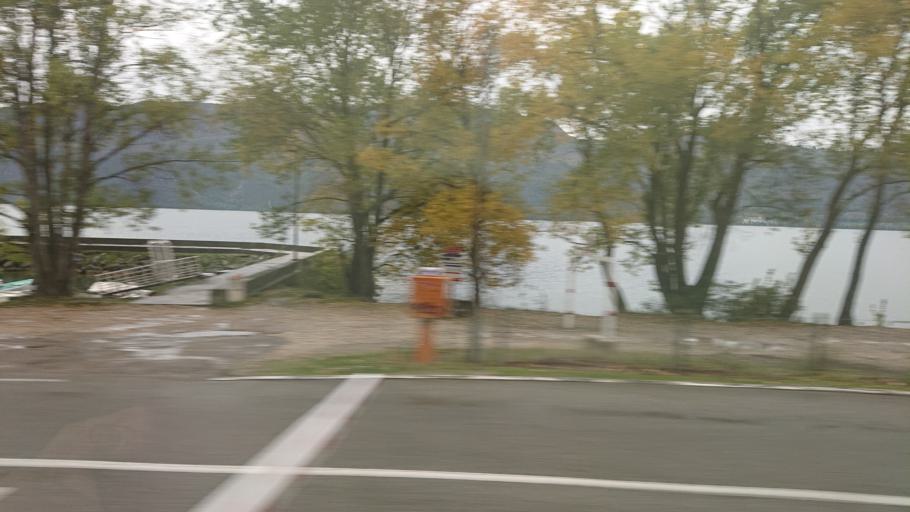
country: FR
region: Rhone-Alpes
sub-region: Departement de la Savoie
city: Brison-Saint-Innocent
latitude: 45.7530
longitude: 5.8801
